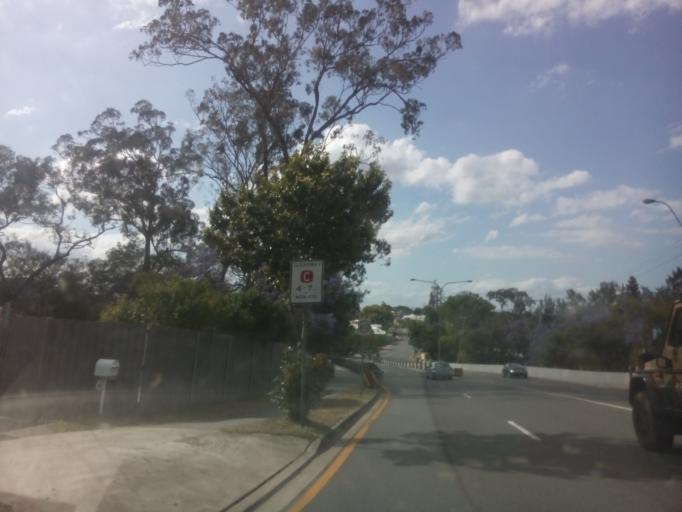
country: AU
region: Queensland
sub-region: Brisbane
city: Milton
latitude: -27.4499
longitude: 153.0005
